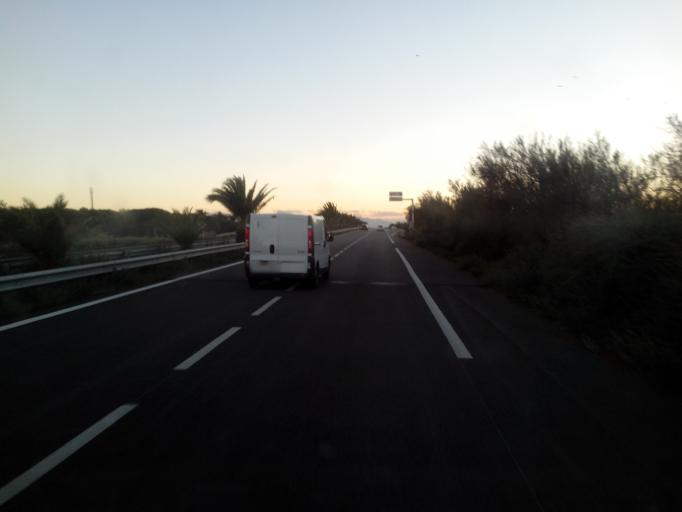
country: FR
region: Languedoc-Roussillon
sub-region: Departement des Pyrenees-Orientales
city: Le Barcares
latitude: 42.8270
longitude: 3.0336
